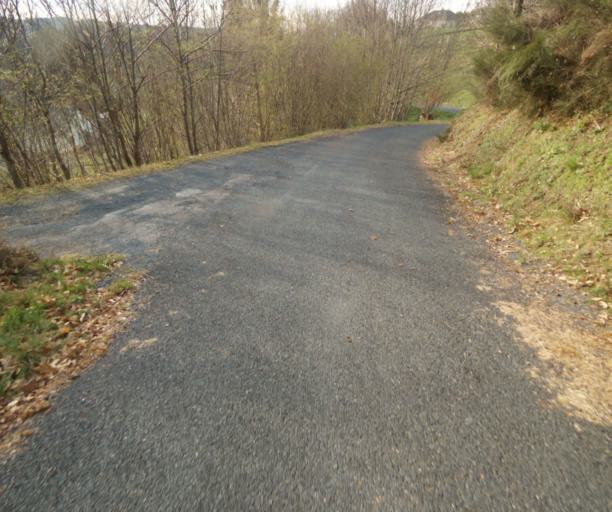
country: FR
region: Limousin
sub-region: Departement de la Correze
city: Correze
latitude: 45.3749
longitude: 1.8711
